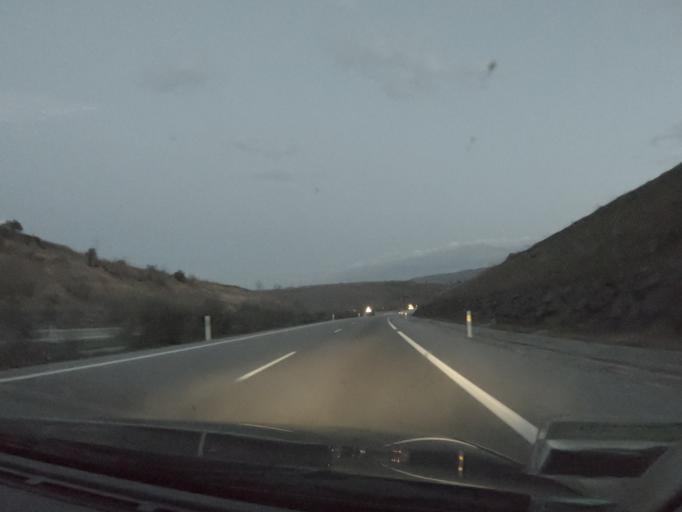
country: ES
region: Castille and Leon
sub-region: Provincia de Leon
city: Bembibre
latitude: 42.6250
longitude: -6.4113
